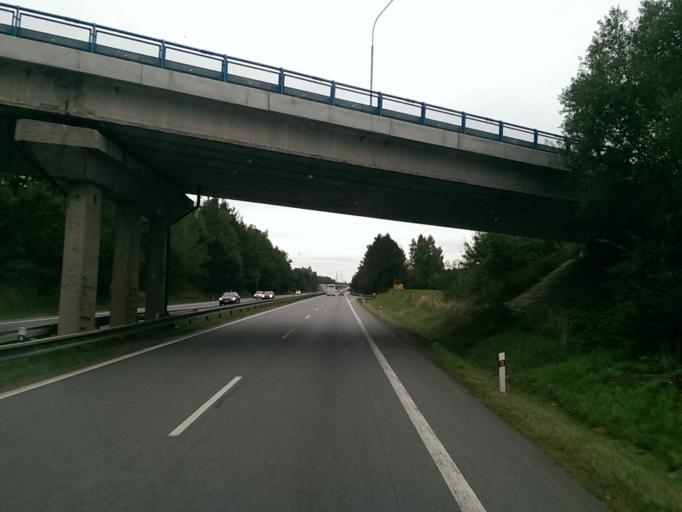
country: CZ
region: Vysocina
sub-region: Okres Jihlava
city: Jihlava
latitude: 49.4426
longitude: 15.6070
